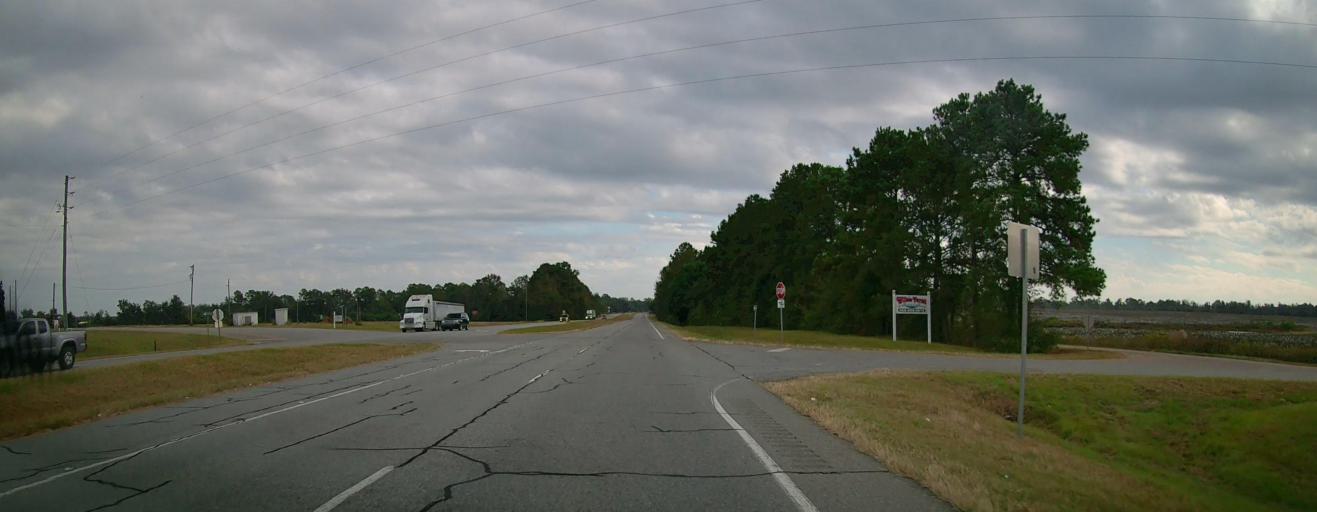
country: US
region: Georgia
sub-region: Thomas County
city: Meigs
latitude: 31.0868
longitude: -84.0883
